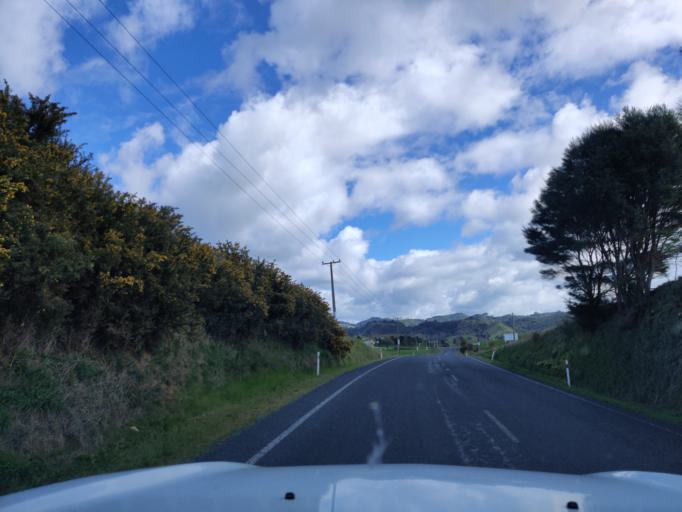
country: NZ
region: Waikato
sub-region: Waikato District
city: Ngaruawahia
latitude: -37.5768
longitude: 175.2339
